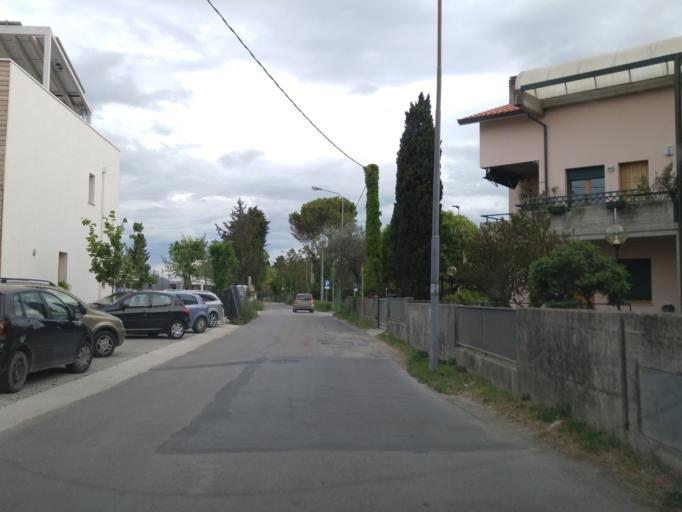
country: IT
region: The Marches
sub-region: Provincia di Pesaro e Urbino
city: Fano
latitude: 43.8309
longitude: 13.0059
